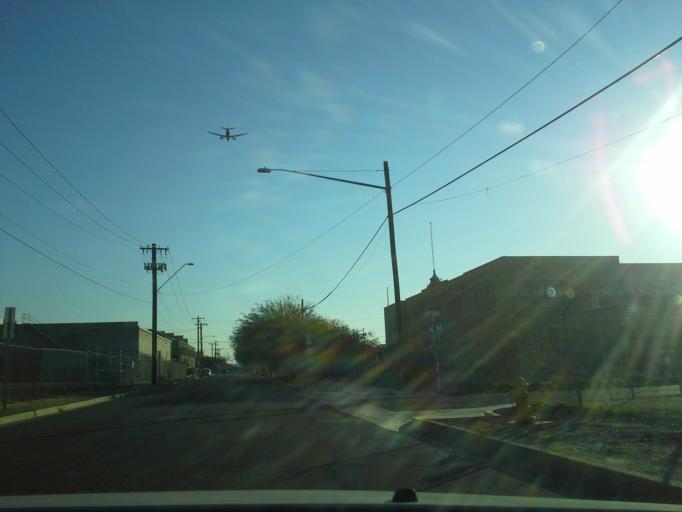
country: US
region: Arizona
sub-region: Maricopa County
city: Phoenix
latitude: 33.4409
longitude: -112.0691
